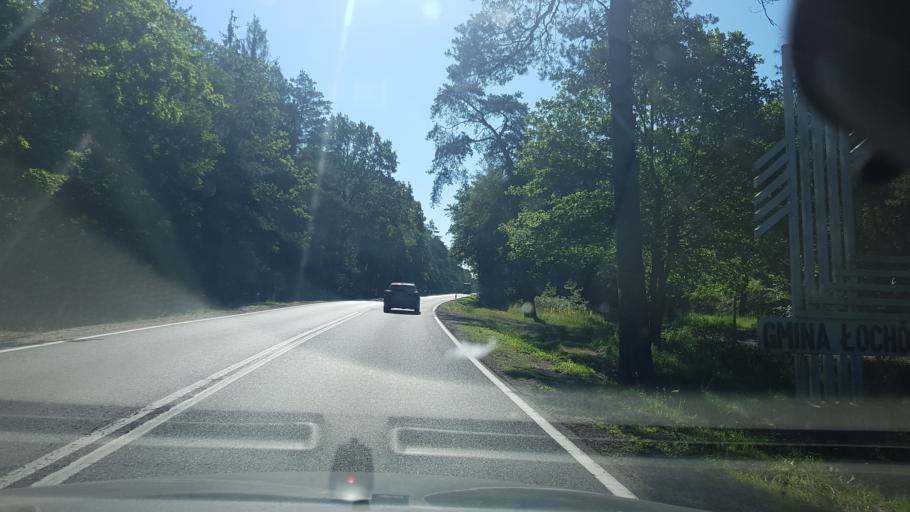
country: PL
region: Masovian Voivodeship
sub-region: Powiat wyszkowski
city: Branszczyk
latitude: 52.5548
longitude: 21.5993
